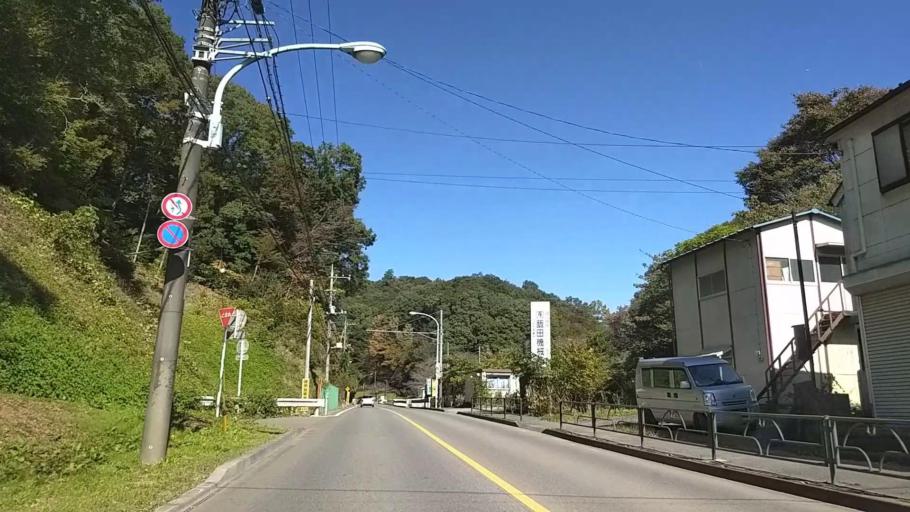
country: JP
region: Tokyo
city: Hachioji
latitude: 35.6155
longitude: 139.2896
